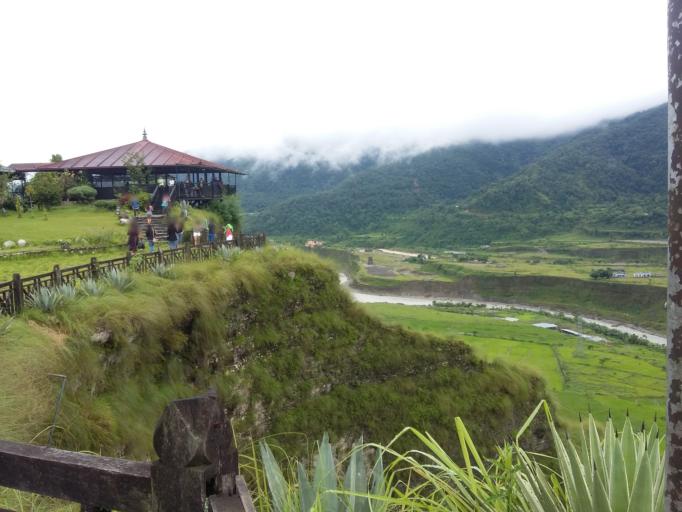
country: NP
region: Western Region
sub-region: Gandaki Zone
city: Pokhara
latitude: 28.1767
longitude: 83.9981
